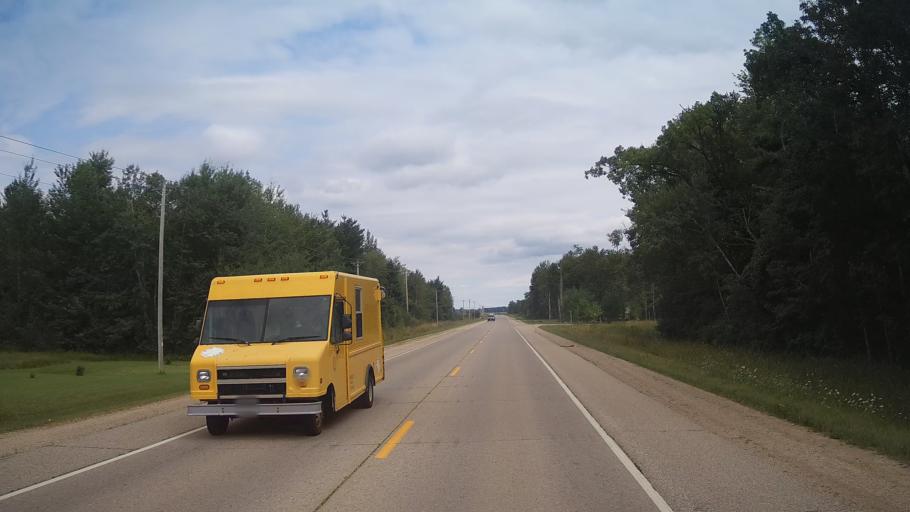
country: US
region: Wisconsin
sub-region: Waushara County
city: Redgranite
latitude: 44.0375
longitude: -89.0735
